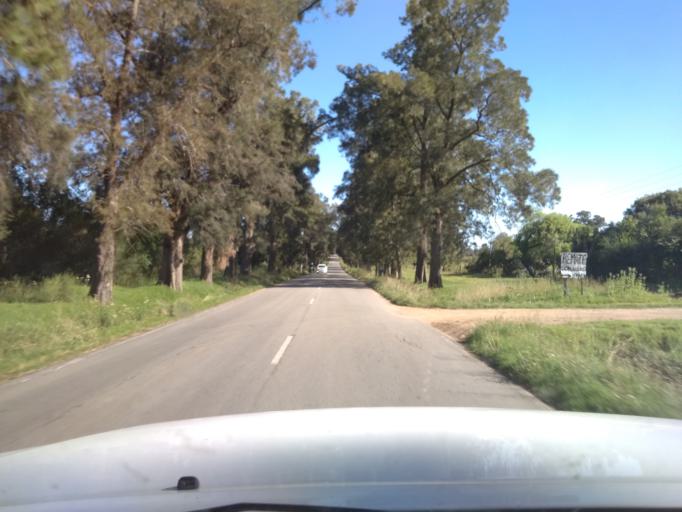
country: UY
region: Canelones
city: San Bautista
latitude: -34.3754
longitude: -55.9595
